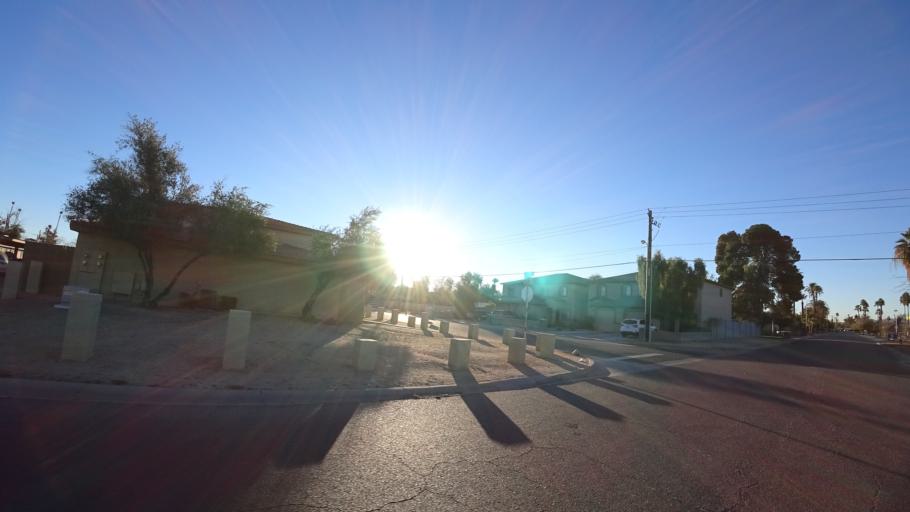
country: US
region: Arizona
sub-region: Maricopa County
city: Paradise Valley
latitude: 33.4844
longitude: -111.9999
